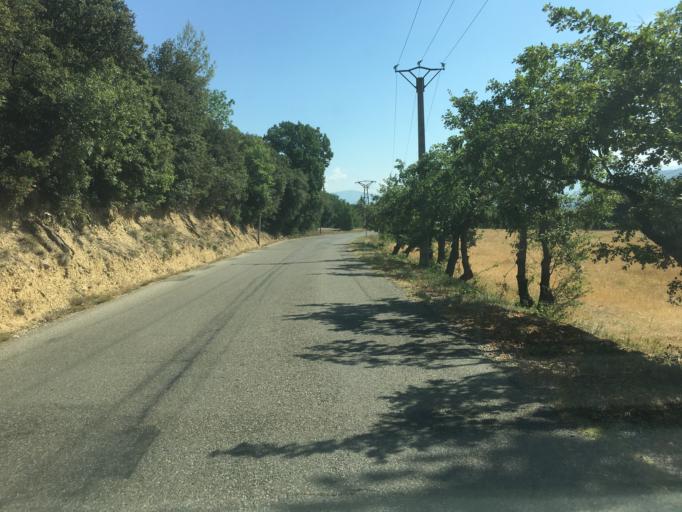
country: FR
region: Provence-Alpes-Cote d'Azur
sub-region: Departement des Alpes-de-Haute-Provence
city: Valensole
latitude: 43.9006
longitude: 6.0228
